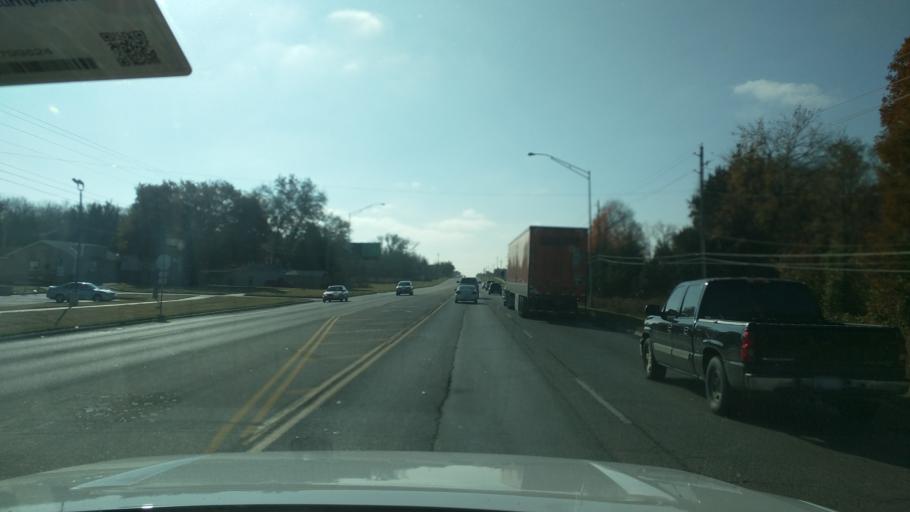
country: US
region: Oklahoma
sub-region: Washington County
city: Bartlesville
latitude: 36.7077
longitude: -95.9352
